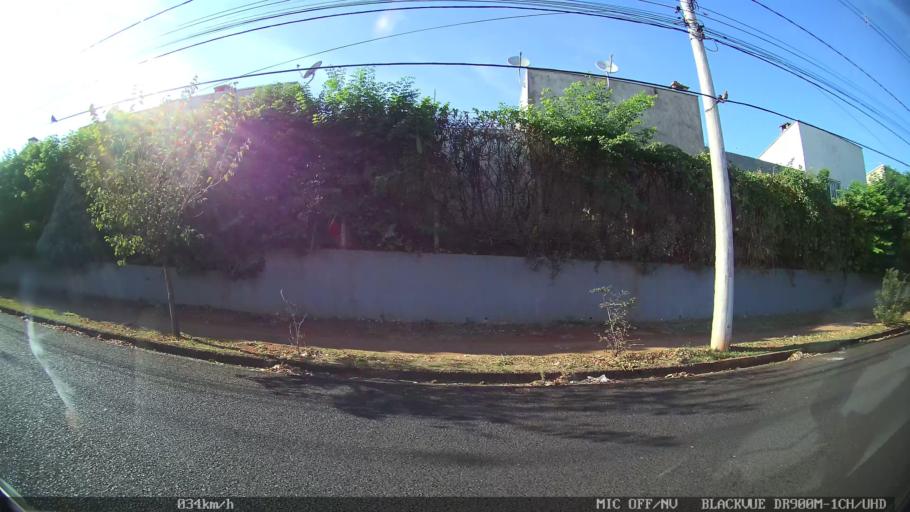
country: BR
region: Sao Paulo
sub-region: Sao Jose Do Rio Preto
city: Sao Jose do Rio Preto
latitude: -20.7713
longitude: -49.3310
